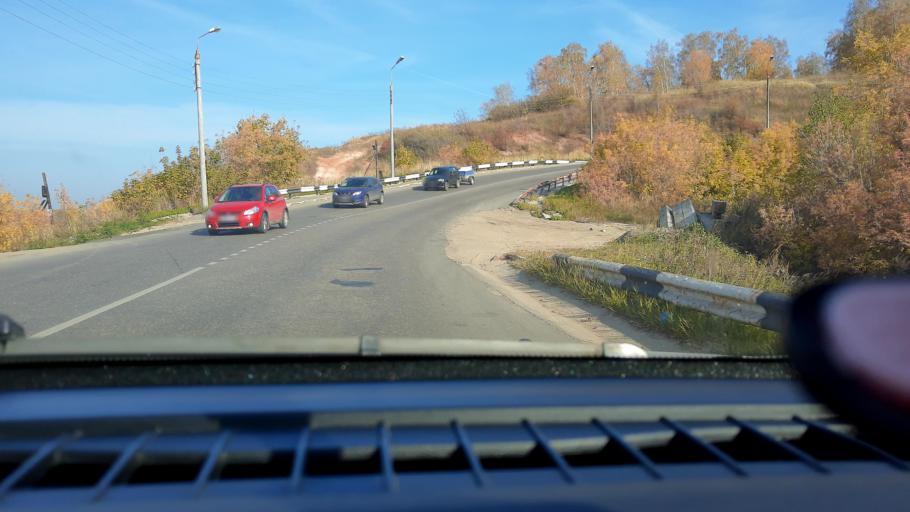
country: RU
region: Nizjnij Novgorod
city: Kstovo
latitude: 56.1570
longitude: 44.2458
